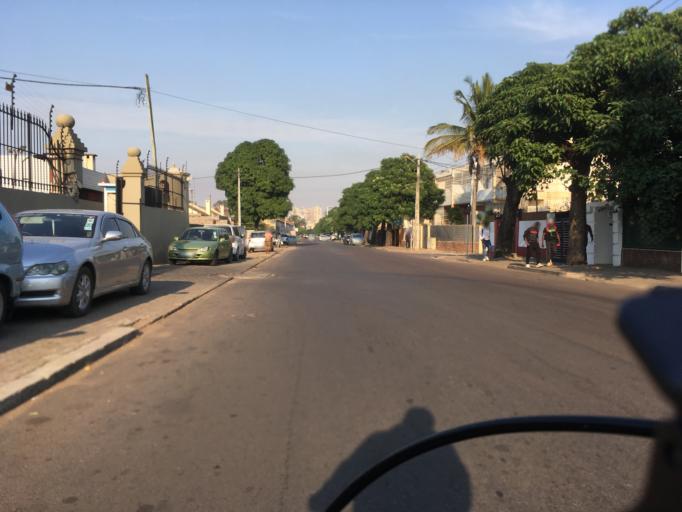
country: MZ
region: Maputo City
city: Maputo
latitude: -25.9567
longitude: 32.5887
